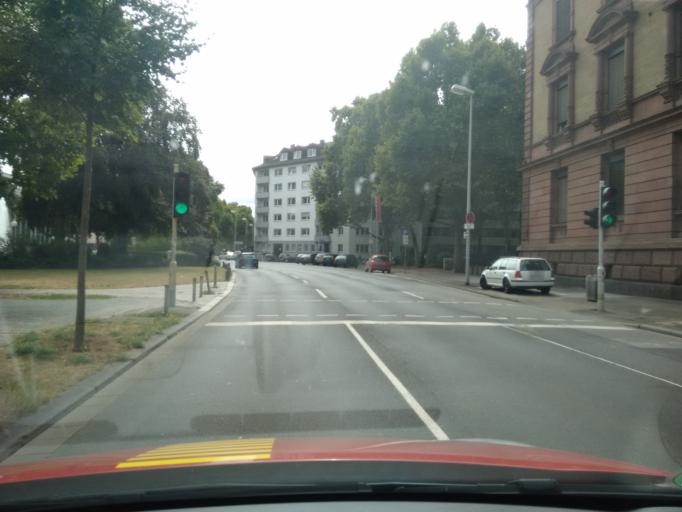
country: DE
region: Rheinland-Pfalz
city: Mainz
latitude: 50.0072
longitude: 8.2658
